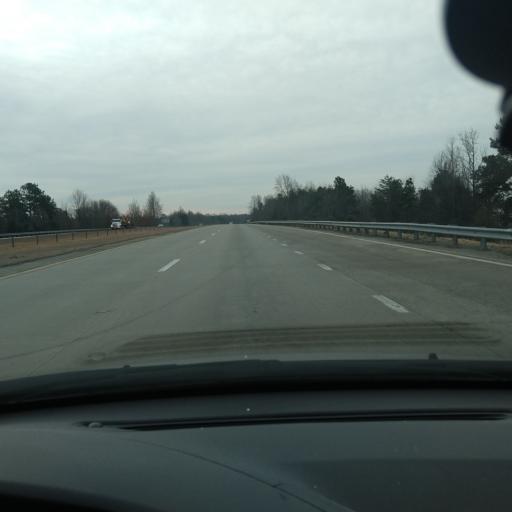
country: US
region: North Carolina
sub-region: Davidson County
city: Midway
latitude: 35.9366
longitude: -80.2336
